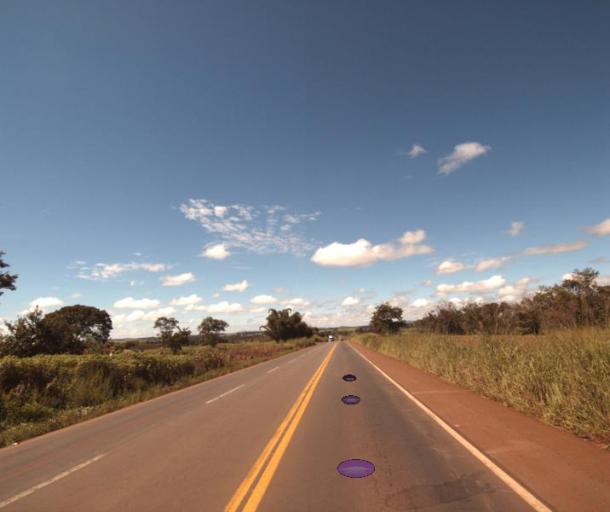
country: BR
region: Goias
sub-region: Rialma
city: Rialma
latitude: -15.3791
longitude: -49.5547
